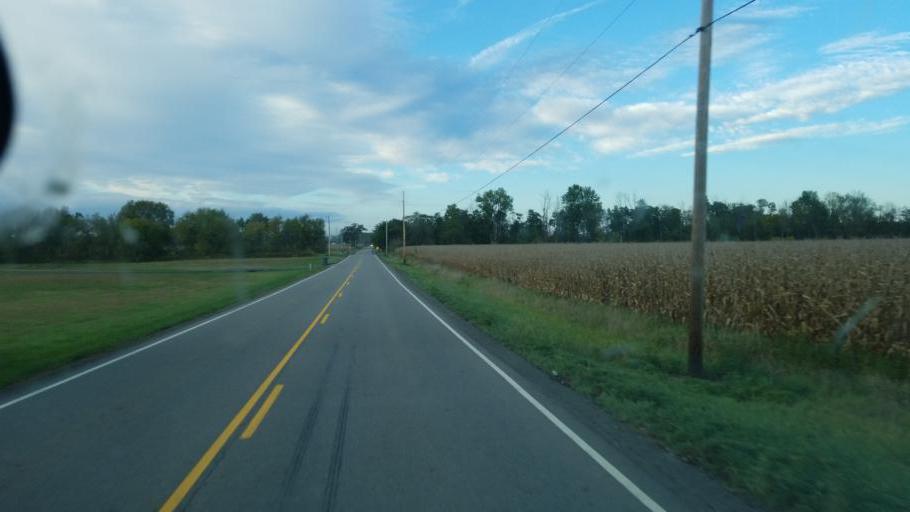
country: US
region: Ohio
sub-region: Licking County
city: Utica
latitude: 40.2624
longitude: -82.5171
